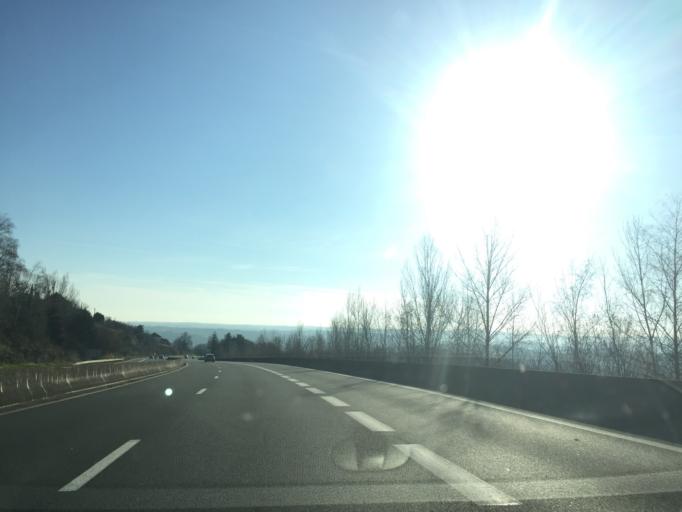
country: FR
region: Limousin
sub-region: Departement de la Correze
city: Donzenac
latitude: 45.2377
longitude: 1.5127
